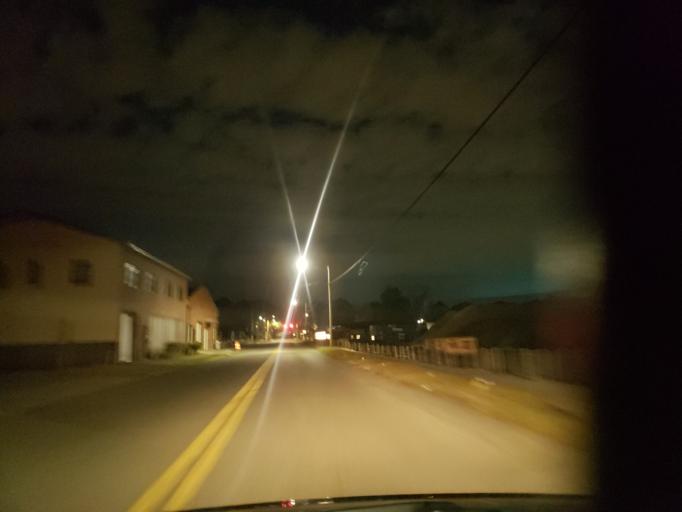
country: US
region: Georgia
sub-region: Chatham County
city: Thunderbolt
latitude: 32.0572
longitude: -81.0594
